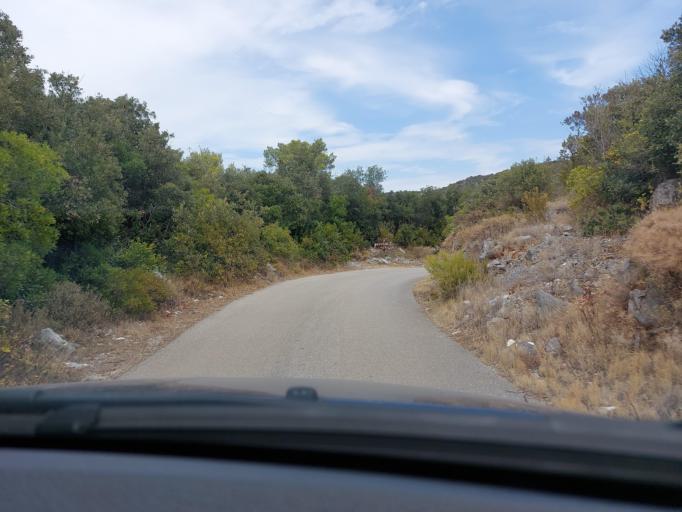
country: HR
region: Dubrovacko-Neretvanska
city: Smokvica
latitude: 42.7615
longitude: 16.9134
